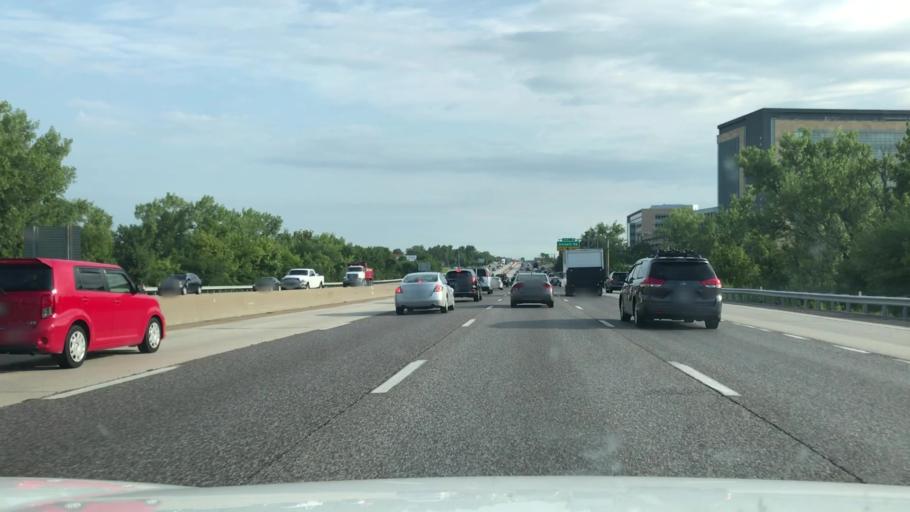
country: US
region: Missouri
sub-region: Saint Louis County
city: Maryland Heights
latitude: 38.7072
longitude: -90.4490
